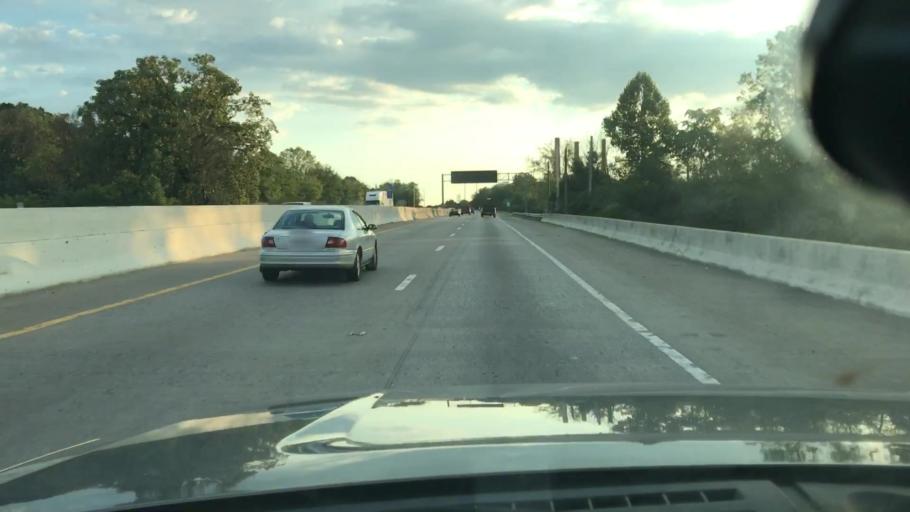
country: US
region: Tennessee
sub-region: Davidson County
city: Nashville
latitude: 36.1836
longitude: -86.8658
